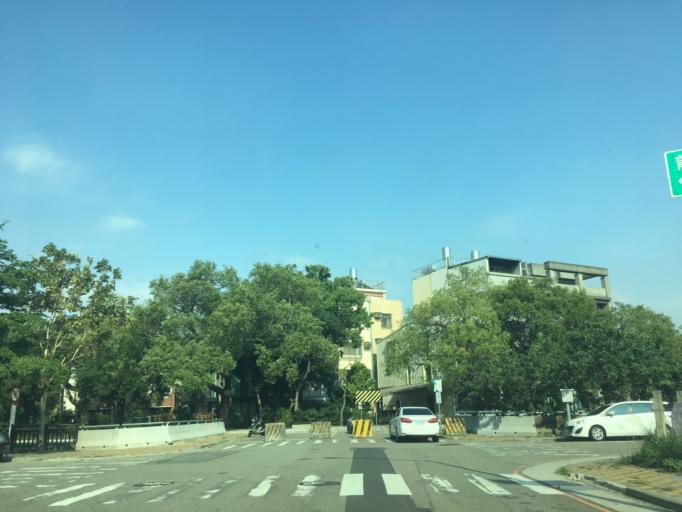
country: TW
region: Taiwan
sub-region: Taichung City
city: Taichung
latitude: 24.1573
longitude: 120.6295
